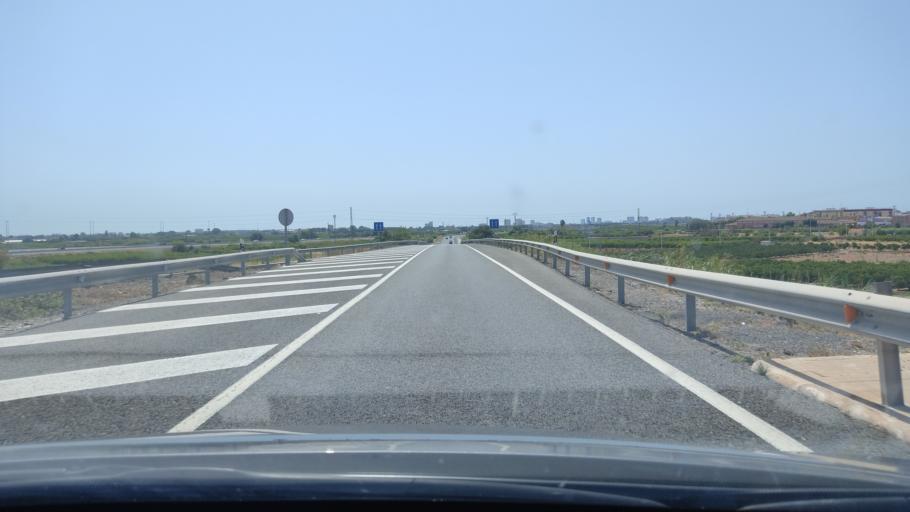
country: ES
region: Valencia
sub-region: Provincia de Valencia
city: Pucol
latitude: 39.6251
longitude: -0.2994
